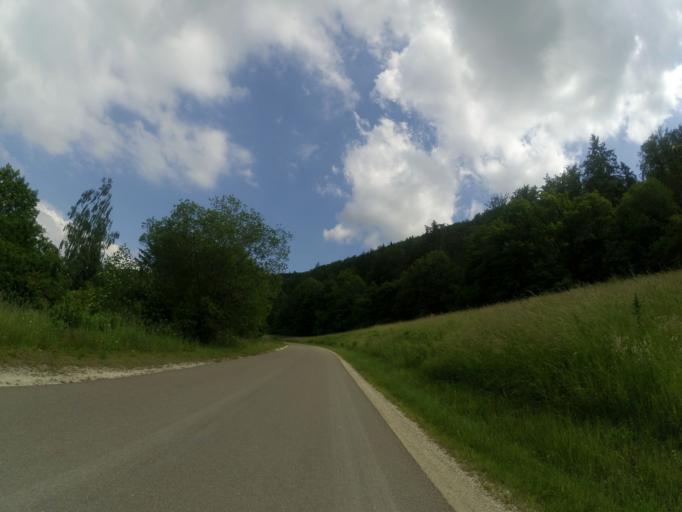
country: DE
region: Baden-Wuerttemberg
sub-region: Tuebingen Region
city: Blaubeuren
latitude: 48.4003
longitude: 9.7824
